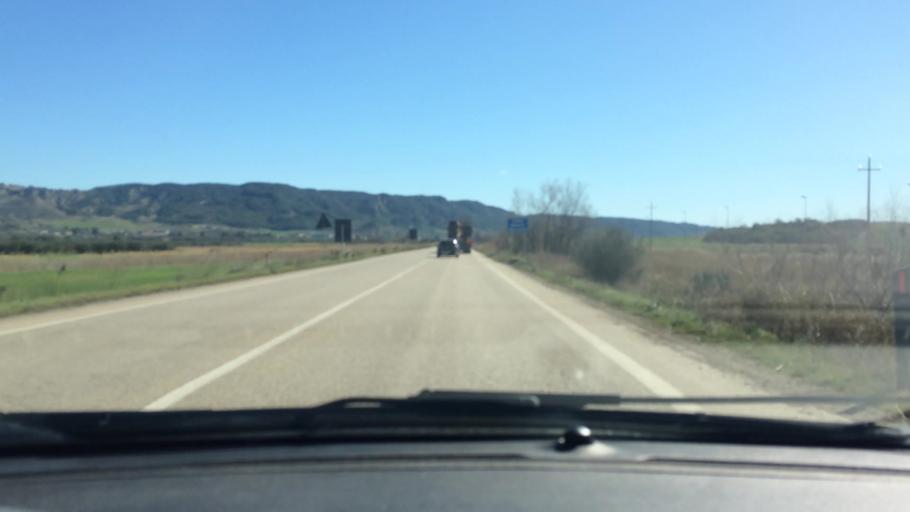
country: IT
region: Basilicate
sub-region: Provincia di Matera
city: Montescaglioso
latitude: 40.5314
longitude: 16.6152
